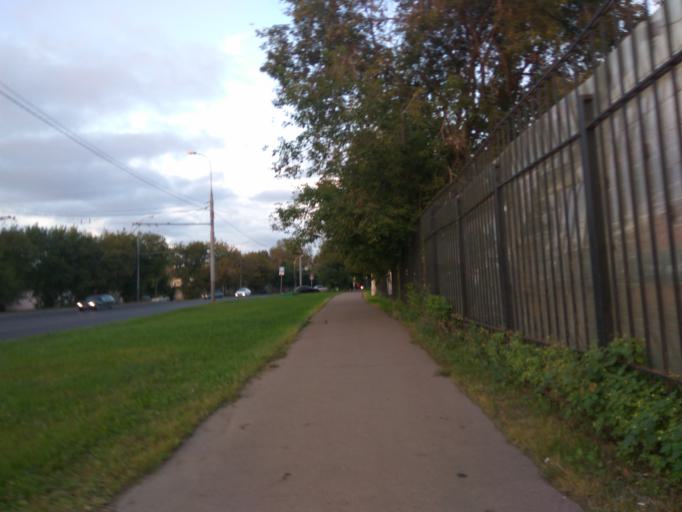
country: RU
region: Moscow
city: Mar'ino
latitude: 55.6586
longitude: 37.7330
